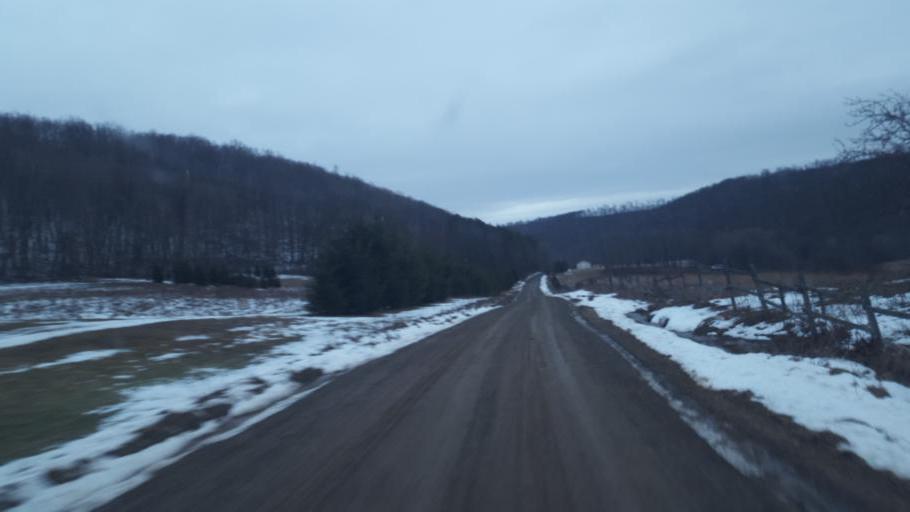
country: US
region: Pennsylvania
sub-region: Potter County
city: Coudersport
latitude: 41.8925
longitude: -77.8316
